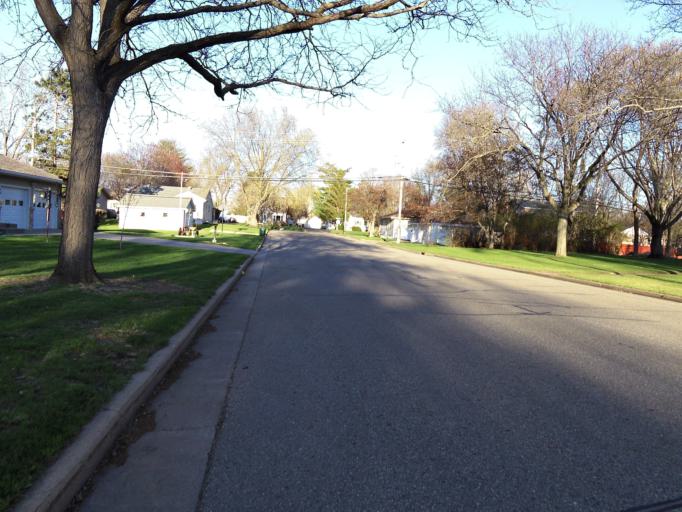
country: US
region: Wisconsin
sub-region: Saint Croix County
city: Hudson
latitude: 44.9679
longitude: -92.7450
